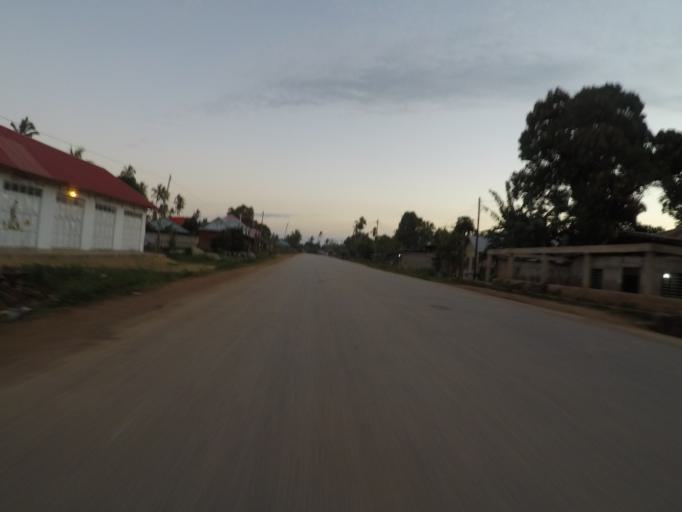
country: TZ
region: Zanzibar Central/South
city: Koani
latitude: -6.0454
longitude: 39.2274
